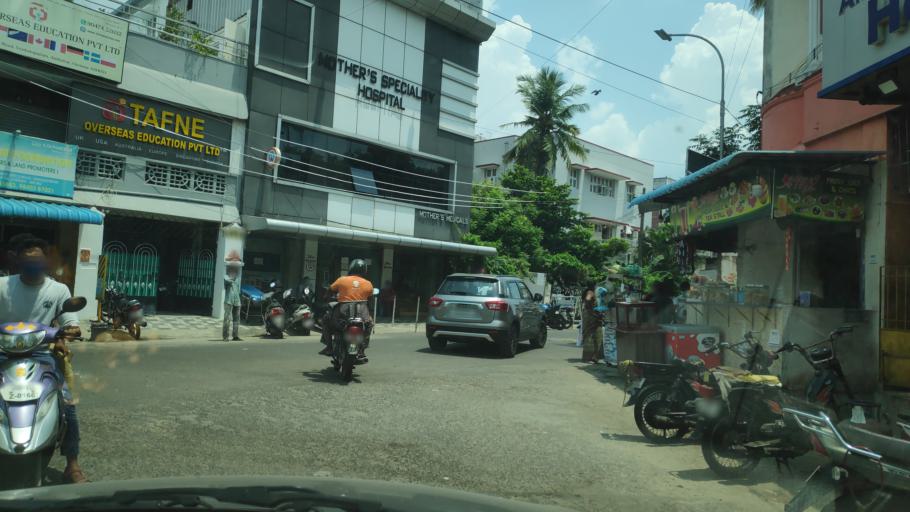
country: IN
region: Tamil Nadu
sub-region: Thiruvallur
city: Ambattur
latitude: 13.1210
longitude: 80.1497
